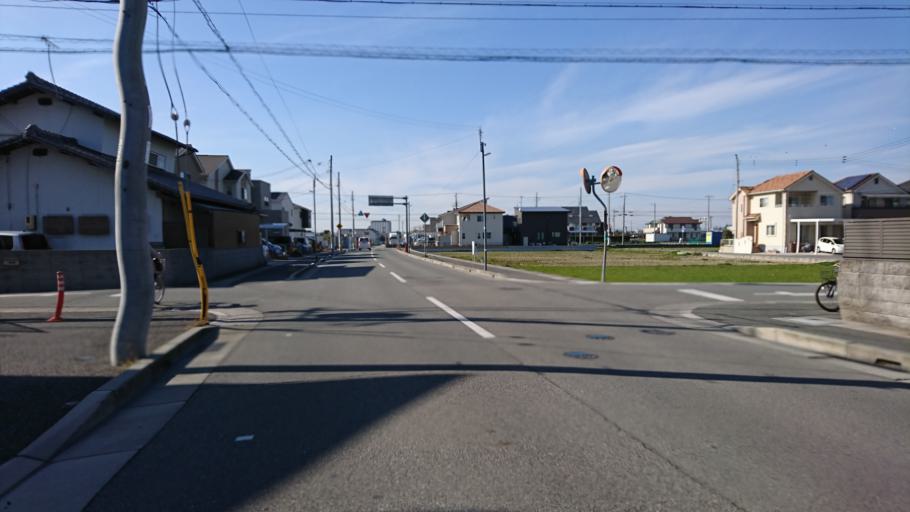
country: JP
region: Hyogo
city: Kakogawacho-honmachi
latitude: 34.7247
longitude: 134.8752
